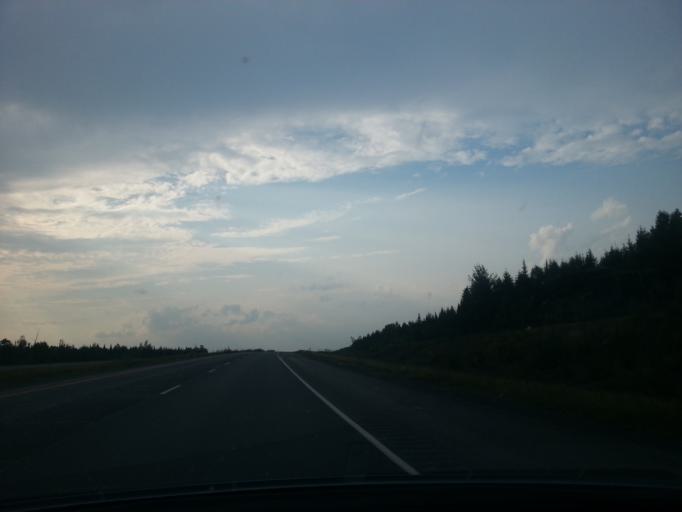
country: CA
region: New Brunswick
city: Harrison Brook
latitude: 47.3049
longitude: -68.0811
